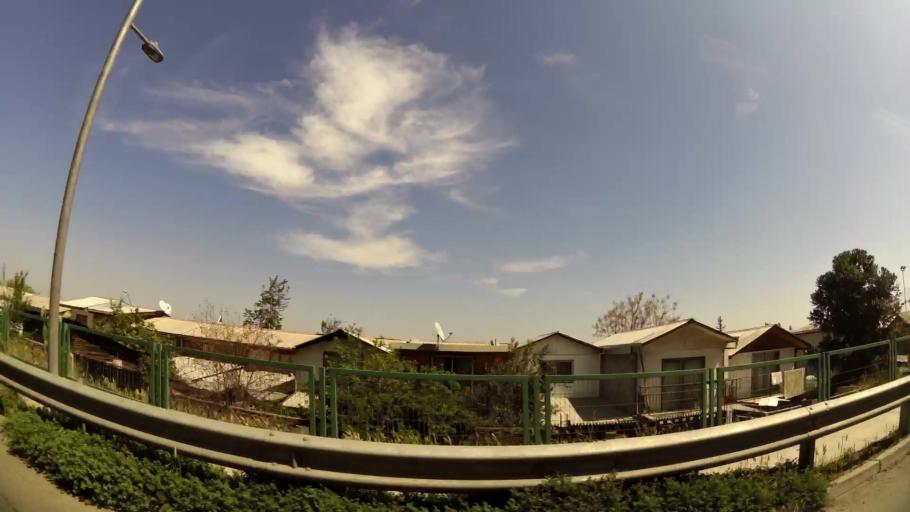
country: CL
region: Santiago Metropolitan
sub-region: Provincia de Santiago
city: Villa Presidente Frei, Nunoa, Santiago, Chile
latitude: -33.4564
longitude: -70.5296
